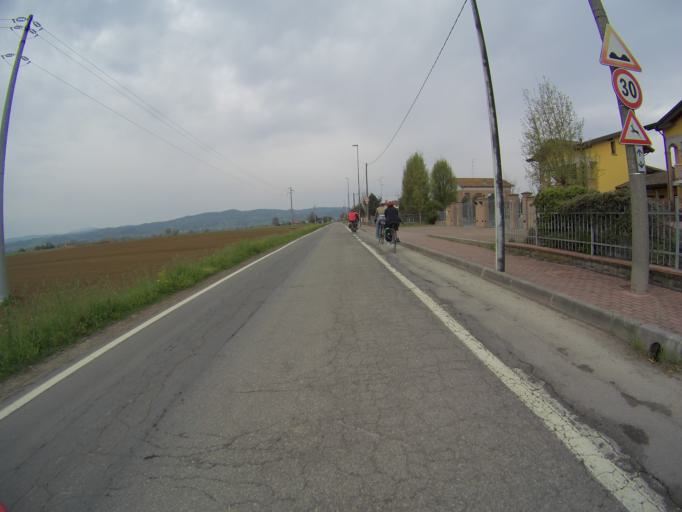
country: IT
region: Emilia-Romagna
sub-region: Provincia di Reggio Emilia
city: Barco
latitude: 44.6635
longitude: 10.4992
